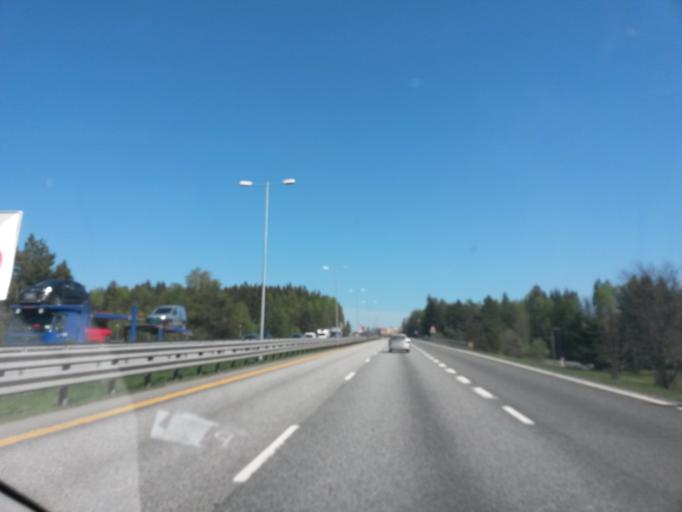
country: NO
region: Buskerud
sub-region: Lier
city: Tranby
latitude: 59.8076
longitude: 10.2848
